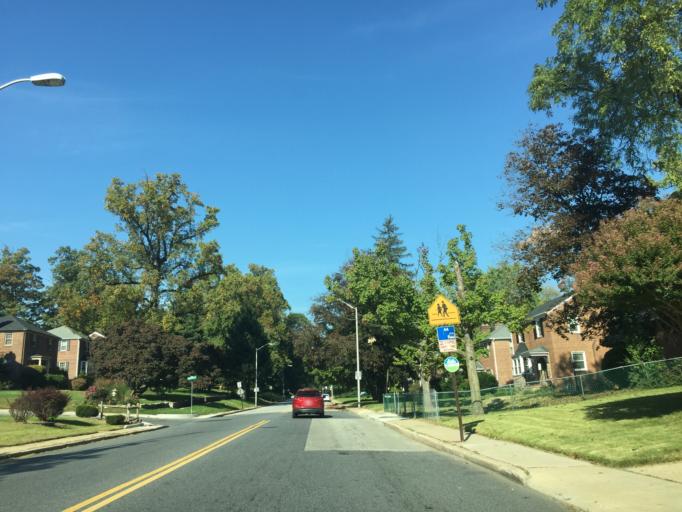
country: US
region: Maryland
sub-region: Baltimore County
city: Towson
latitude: 39.3604
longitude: -76.6009
